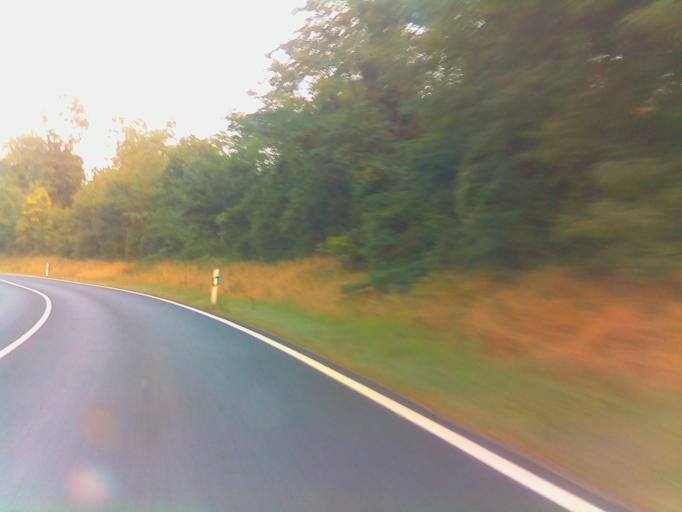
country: DE
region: Bavaria
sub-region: Regierungsbezirk Unterfranken
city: Oerlenbach
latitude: 50.1503
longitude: 10.1062
